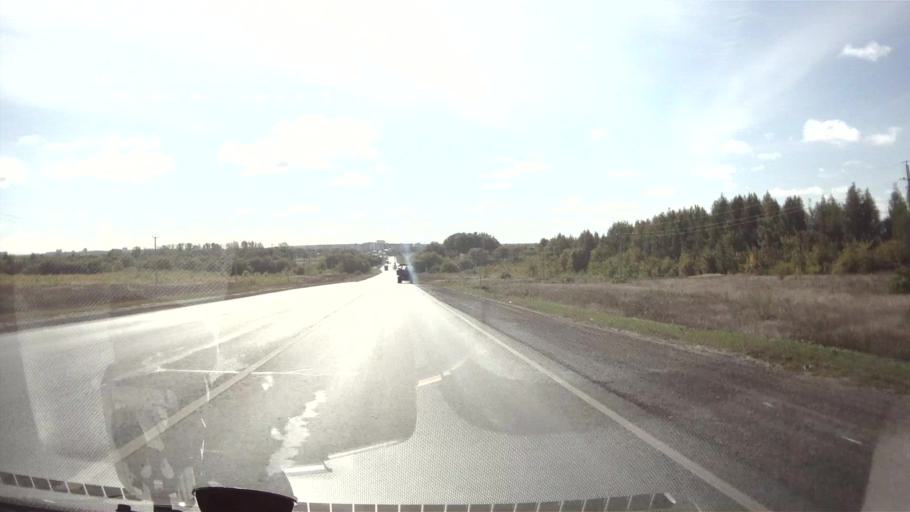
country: RU
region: Ulyanovsk
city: Isheyevka
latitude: 54.3085
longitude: 48.2383
